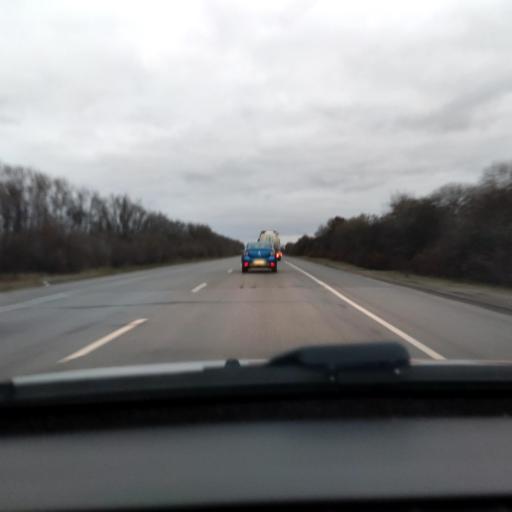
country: RU
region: Lipetsk
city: Borinskoye
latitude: 52.4496
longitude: 39.2939
